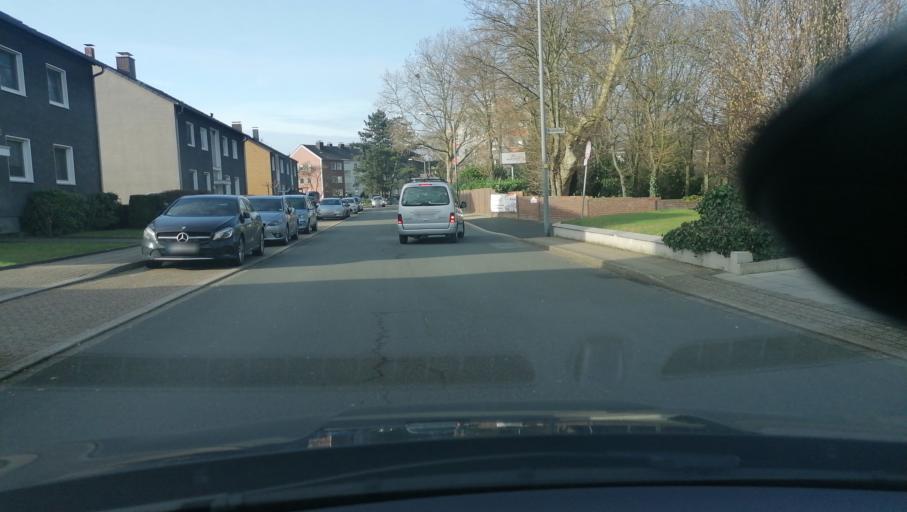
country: DE
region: North Rhine-Westphalia
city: Herten
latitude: 51.6060
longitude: 7.1576
